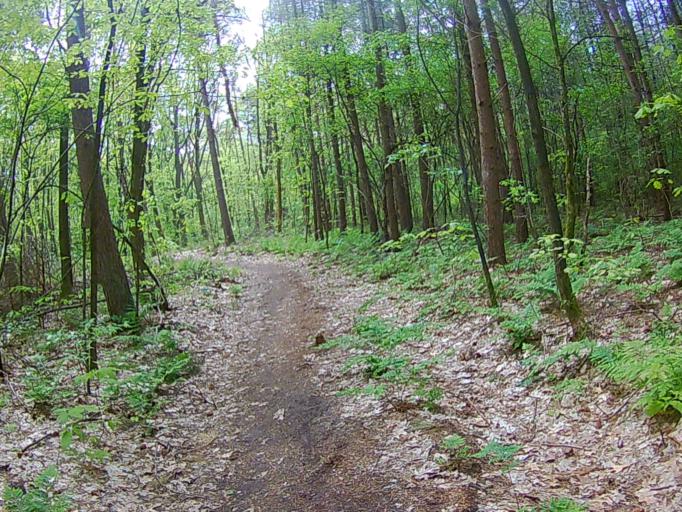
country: BE
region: Flanders
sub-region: Provincie Antwerpen
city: Grobbendonk
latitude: 51.2026
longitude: 4.7447
